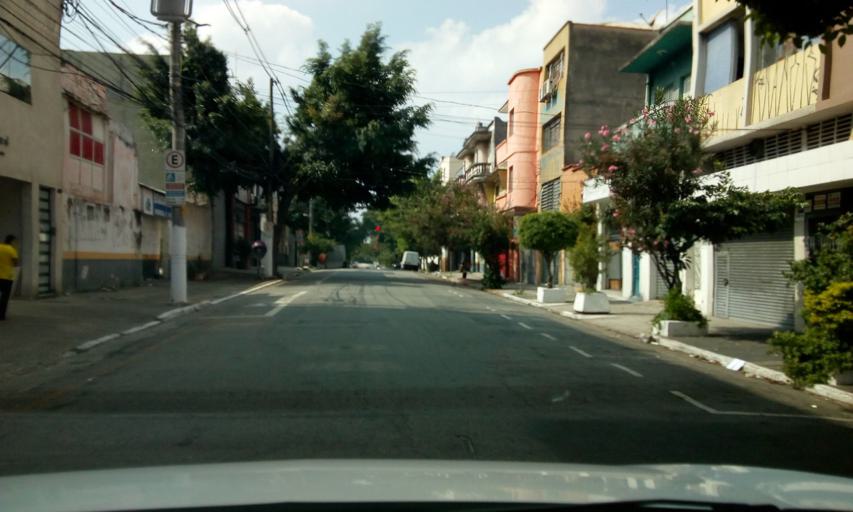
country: BR
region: Sao Paulo
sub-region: Sao Paulo
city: Sao Paulo
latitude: -23.5241
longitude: -46.6414
